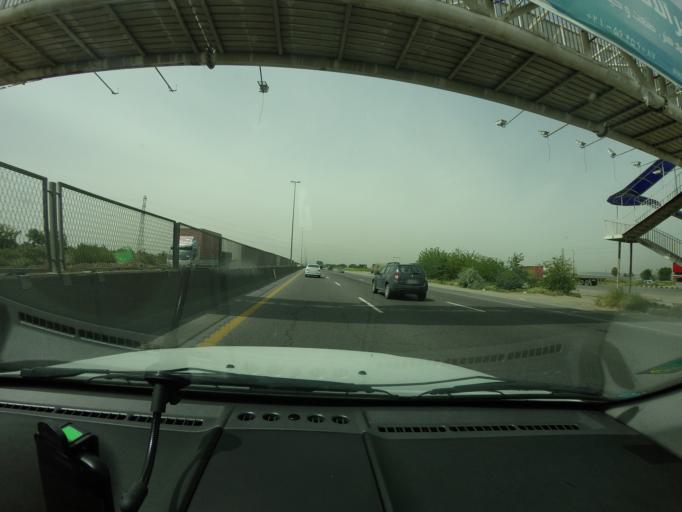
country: IR
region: Tehran
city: Eslamshahr
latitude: 35.6105
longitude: 51.2050
